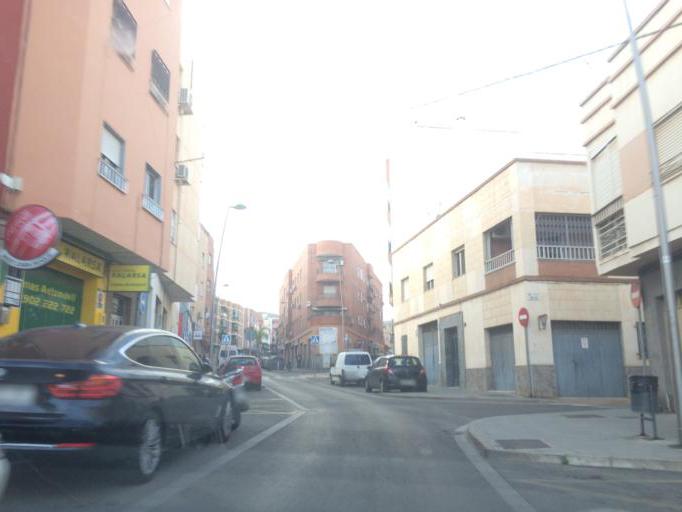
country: ES
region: Andalusia
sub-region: Provincia de Almeria
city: Almeria
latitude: 36.8471
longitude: -2.4679
